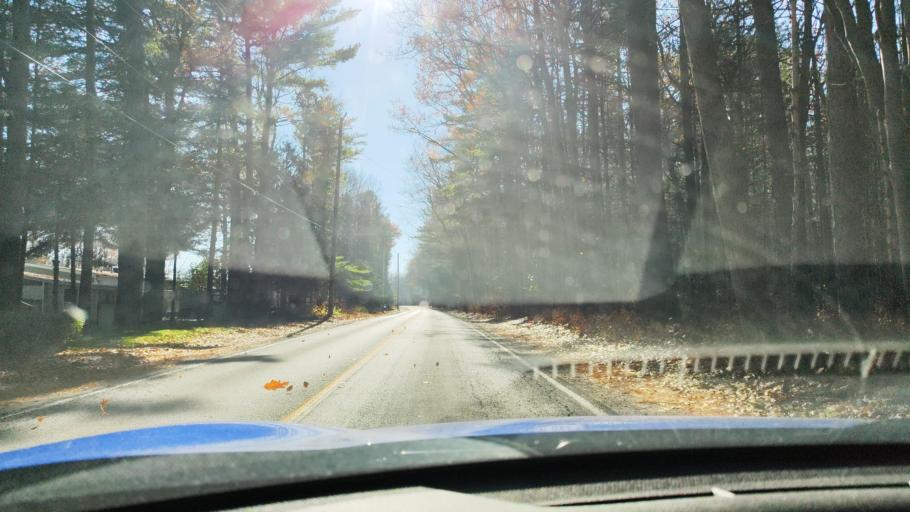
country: CA
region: Ontario
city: Wasaga Beach
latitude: 44.4925
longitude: -80.0047
